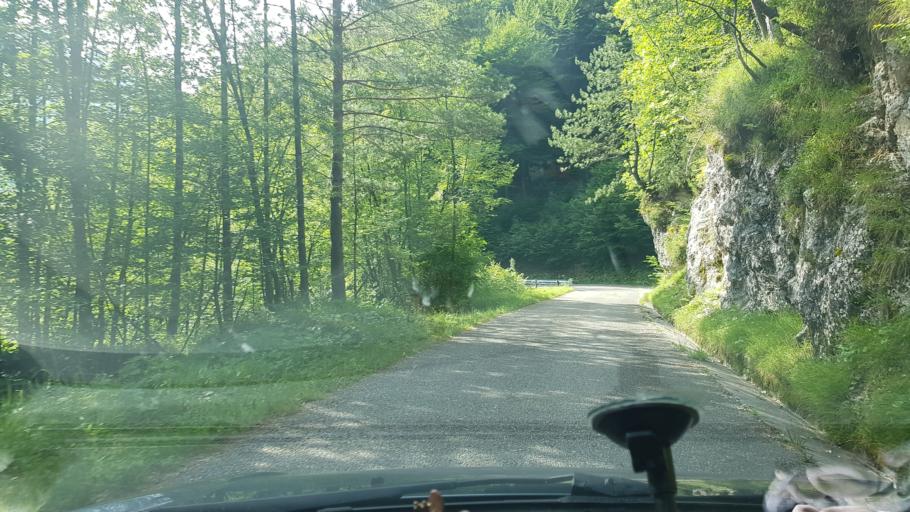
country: IT
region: Friuli Venezia Giulia
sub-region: Provincia di Udine
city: Prato
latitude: 46.3540
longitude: 13.3766
